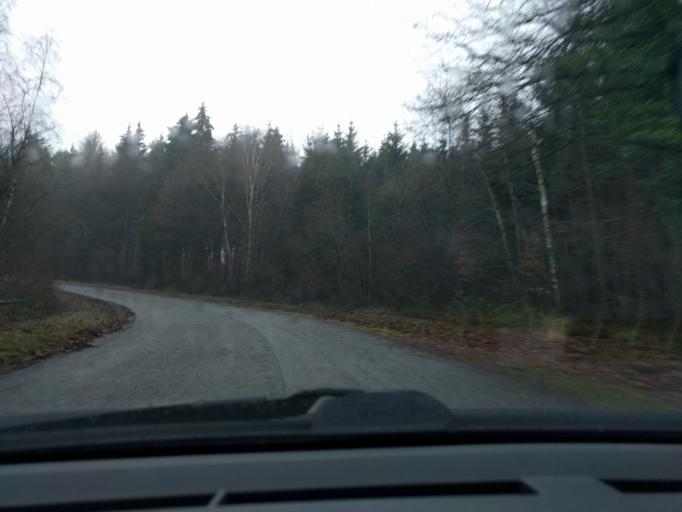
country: BE
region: Wallonia
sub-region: Province de Namur
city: Couvin
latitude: 50.0402
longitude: 4.5369
